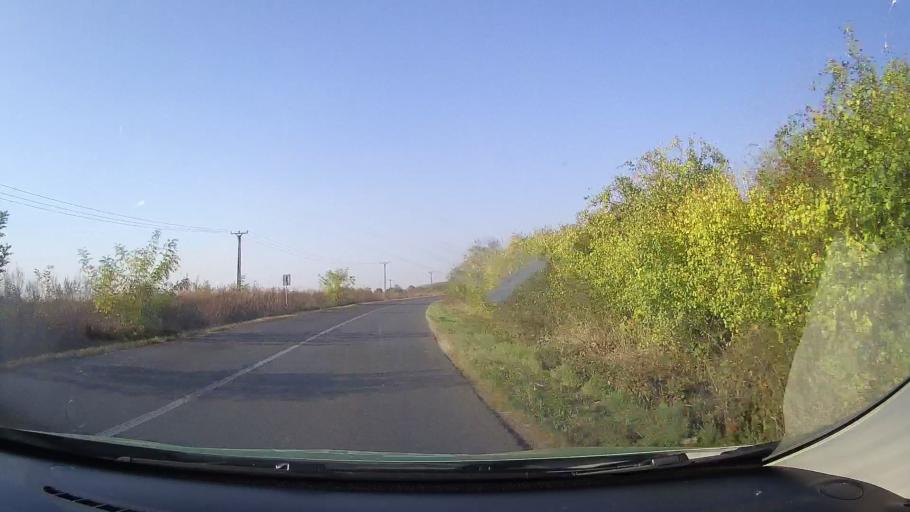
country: RO
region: Arad
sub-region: Comuna Siria
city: Siria
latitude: 46.2397
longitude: 21.6344
